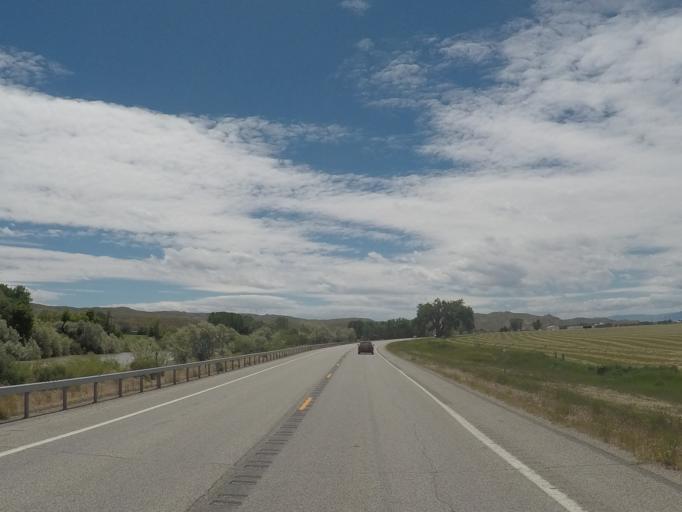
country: US
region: Montana
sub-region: Carbon County
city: Red Lodge
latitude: 45.0964
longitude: -109.0279
